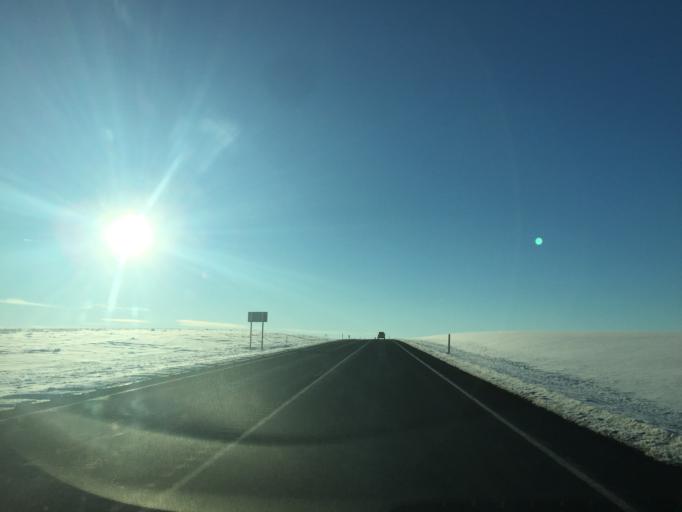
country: US
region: Washington
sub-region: Okanogan County
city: Coulee Dam
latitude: 47.7021
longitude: -118.9505
